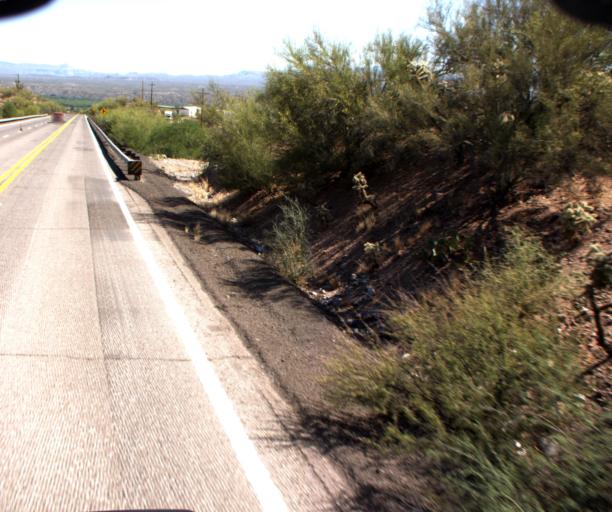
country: US
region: Arizona
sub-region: Pinal County
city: Mammoth
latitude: 32.7054
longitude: -110.6431
